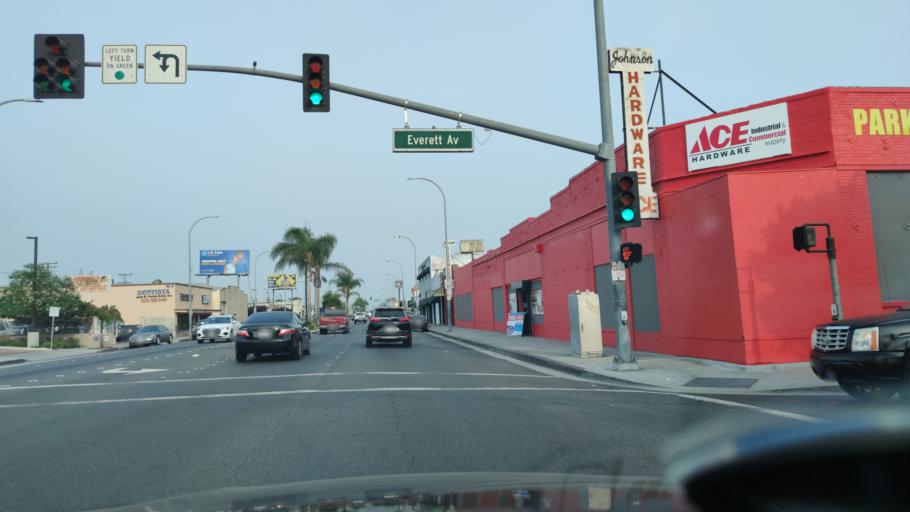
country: US
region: California
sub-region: Los Angeles County
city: Maywood
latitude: 33.9887
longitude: -118.2010
